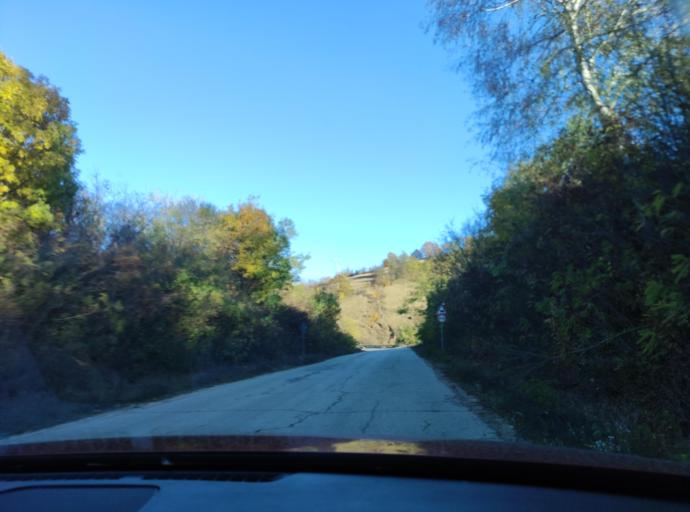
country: BG
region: Montana
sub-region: Obshtina Chiprovtsi
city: Chiprovtsi
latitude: 43.3793
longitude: 22.9120
